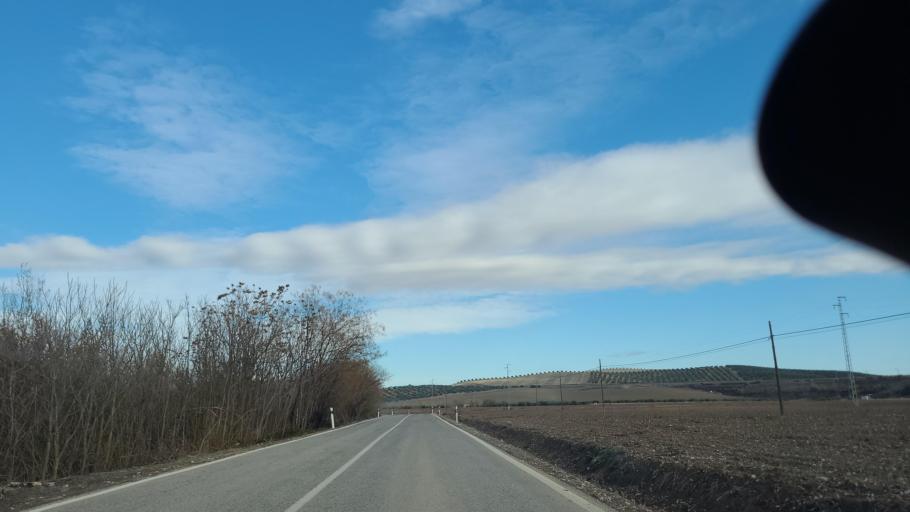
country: ES
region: Andalusia
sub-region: Provincia de Jaen
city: Villanueva de la Reina
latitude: 38.0109
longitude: -3.8966
